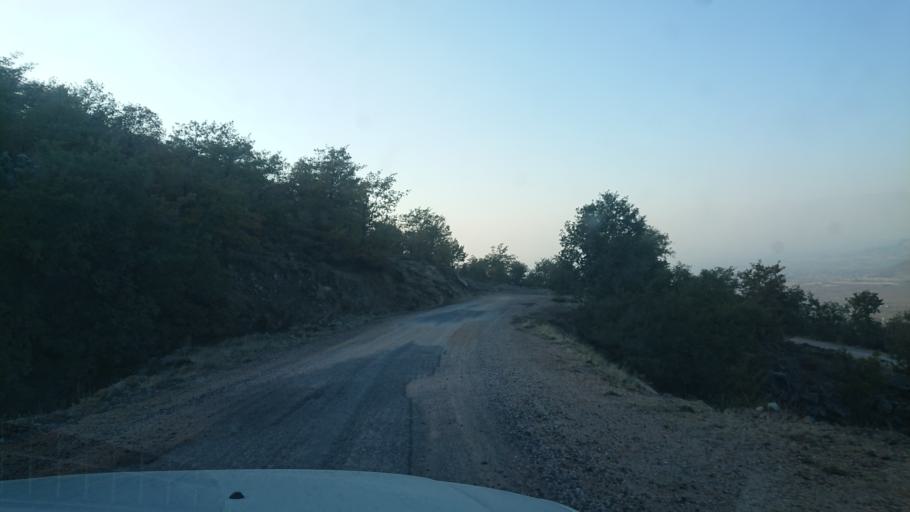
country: TR
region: Aksaray
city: Taspinar
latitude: 38.1704
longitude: 34.1800
